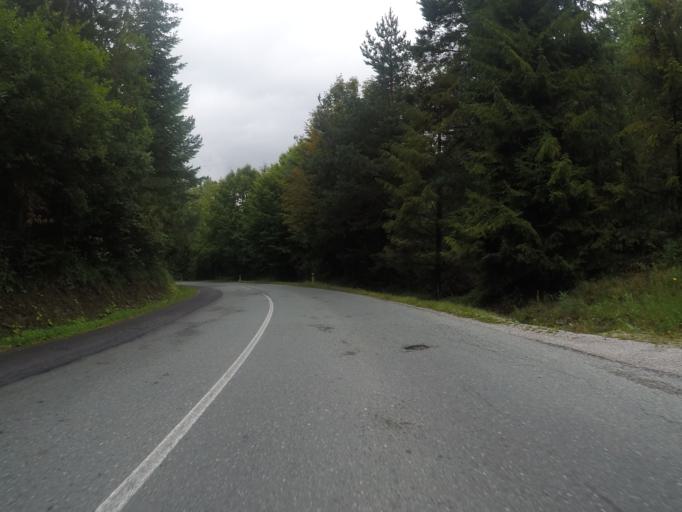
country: SK
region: Kosicky
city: Spisska Nova Ves
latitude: 48.8925
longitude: 20.5336
